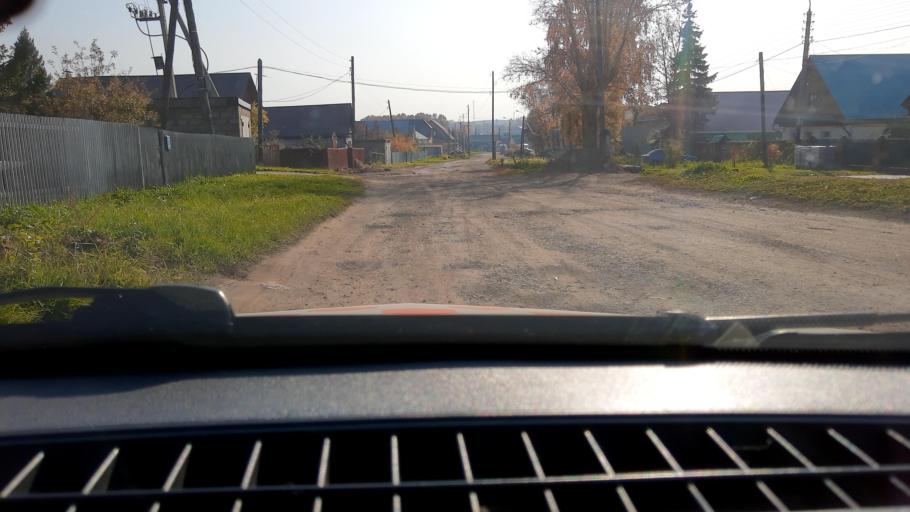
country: RU
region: Bashkortostan
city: Ufa
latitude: 54.8432
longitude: 56.1552
